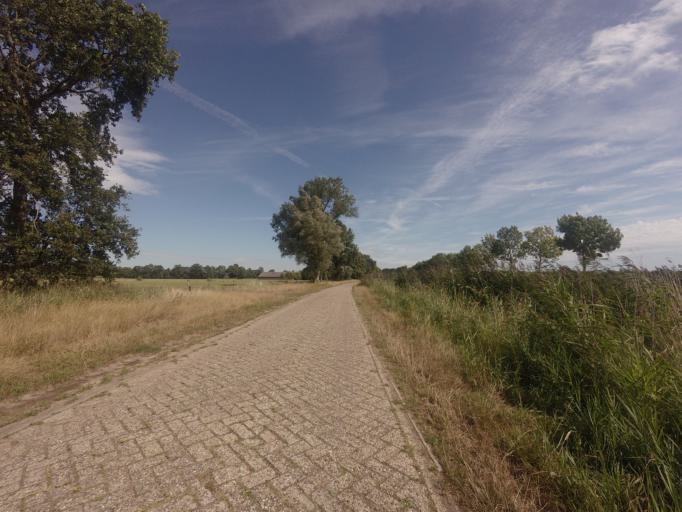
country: NL
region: Overijssel
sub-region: Gemeente Raalte
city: Raalte
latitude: 52.4106
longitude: 6.3116
